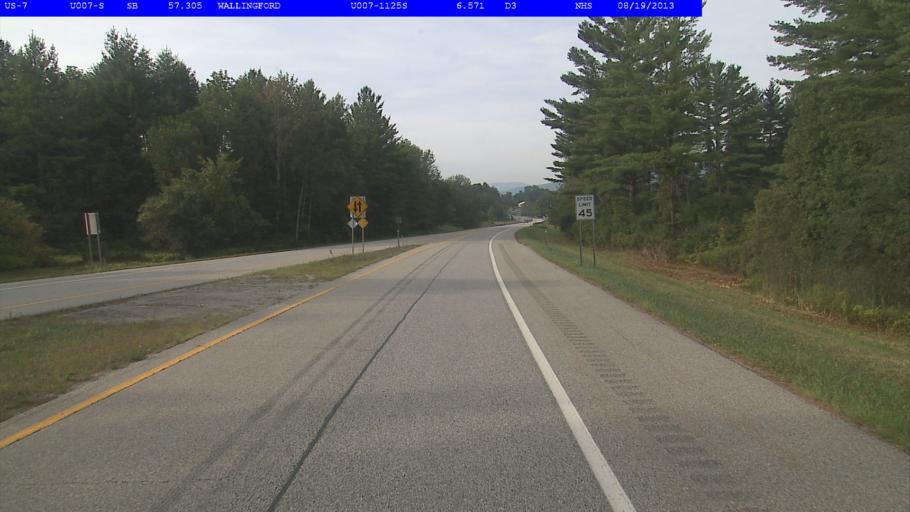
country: US
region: Vermont
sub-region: Rutland County
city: Rutland
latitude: 43.4874
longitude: -72.9713
